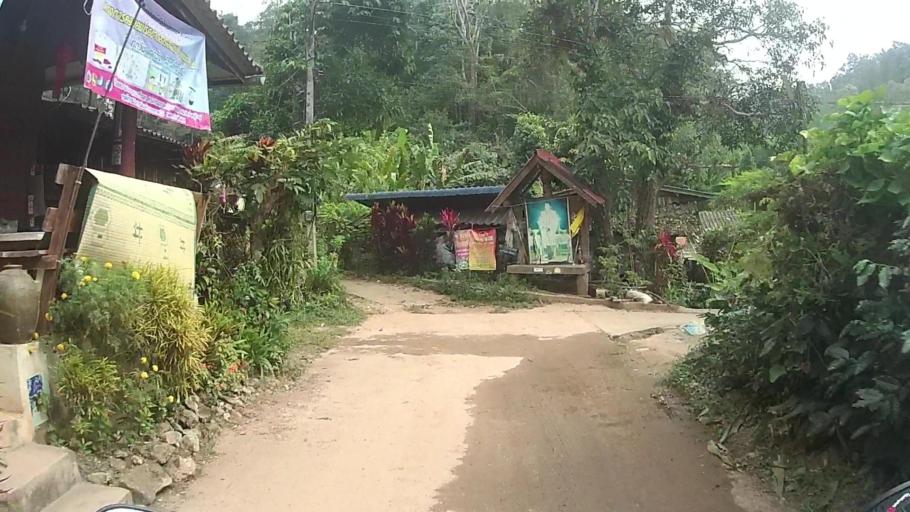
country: TH
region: Chiang Mai
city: Mae On
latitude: 18.7962
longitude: 99.3496
